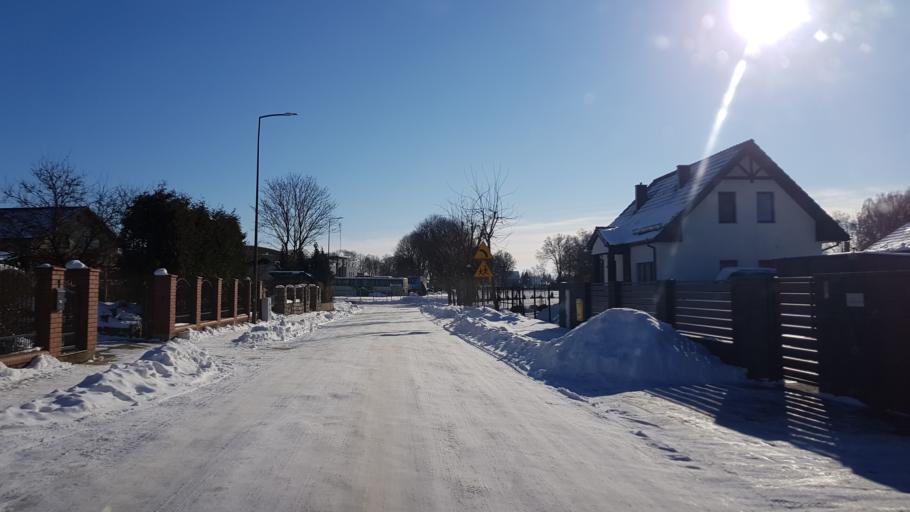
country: PL
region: West Pomeranian Voivodeship
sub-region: Powiat koszalinski
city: Bobolice
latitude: 53.9590
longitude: 16.5910
